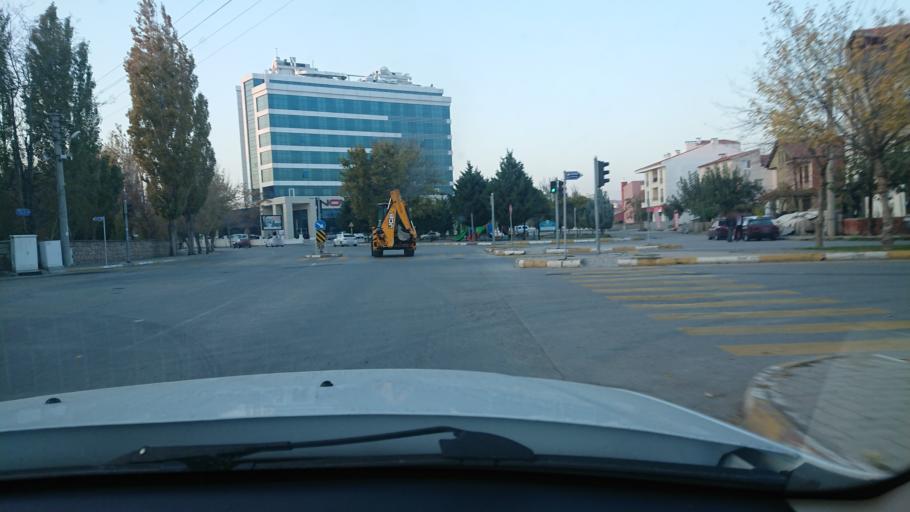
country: TR
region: Aksaray
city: Aksaray
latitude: 38.3577
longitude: 34.0411
